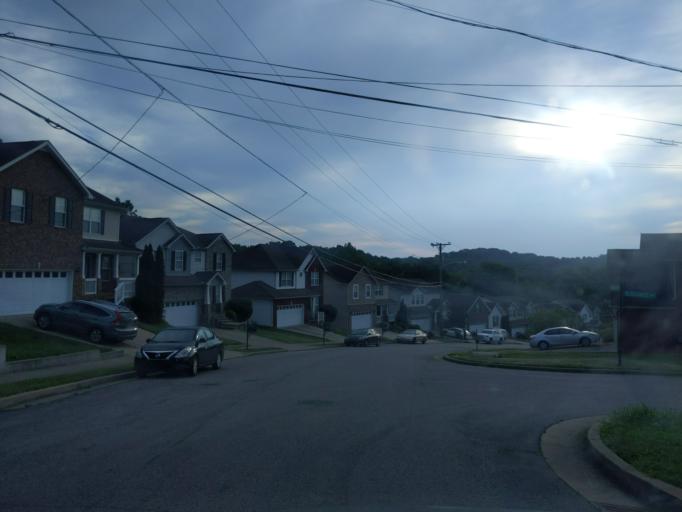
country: US
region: Tennessee
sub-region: Wilson County
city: Green Hill
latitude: 36.1809
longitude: -86.5969
